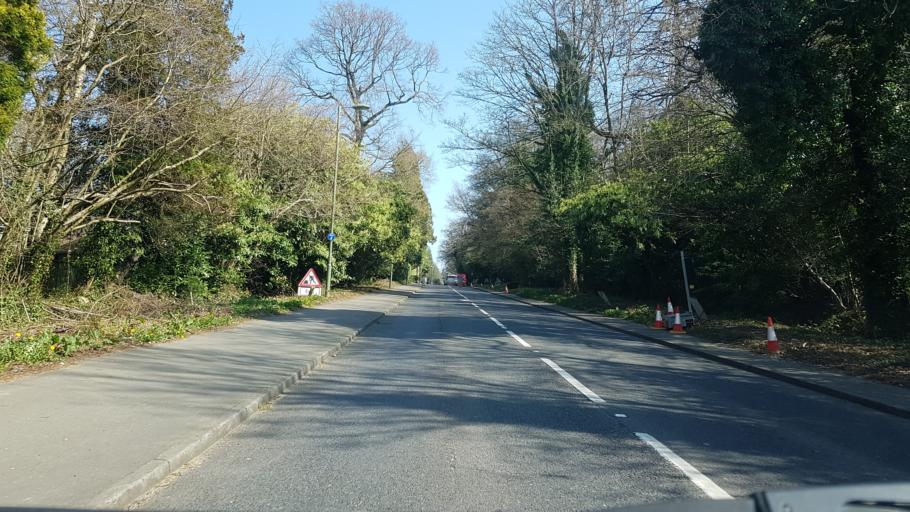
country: GB
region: England
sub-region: Surrey
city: Hindhead
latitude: 51.1090
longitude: -0.7408
